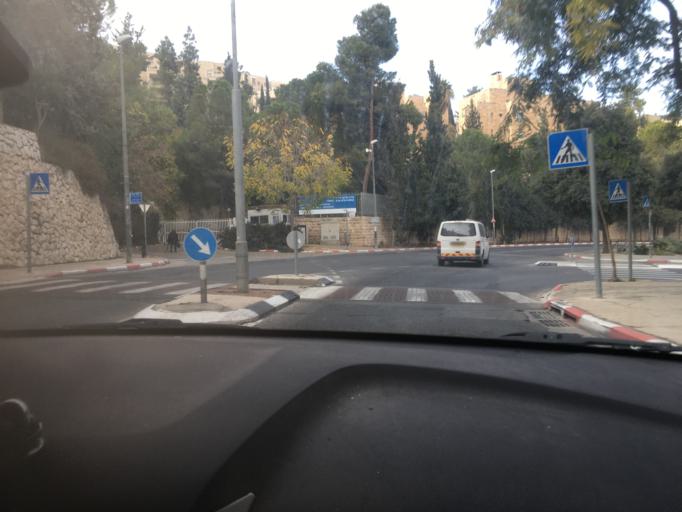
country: IL
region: Jerusalem
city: Jerusalem
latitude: 31.7491
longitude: 35.2327
